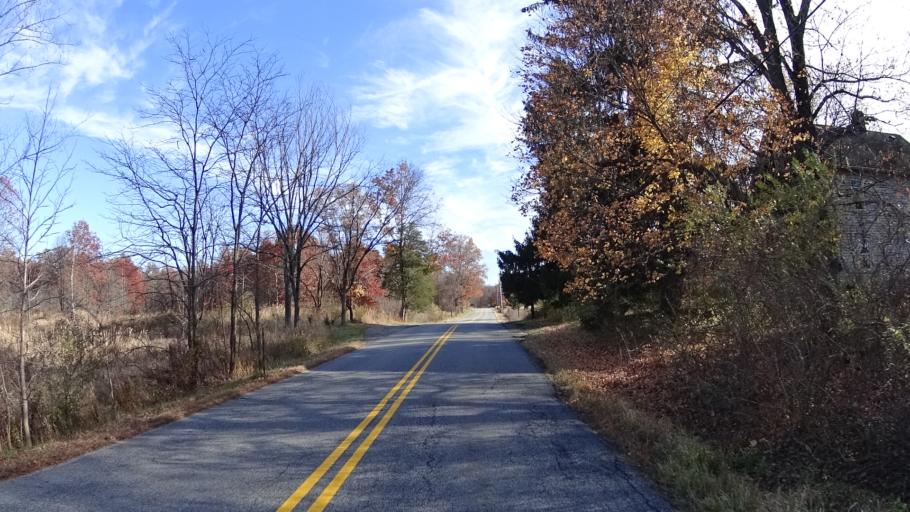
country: US
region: New Jersey
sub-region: Union County
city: Berkeley Heights
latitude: 40.7147
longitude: -74.4858
